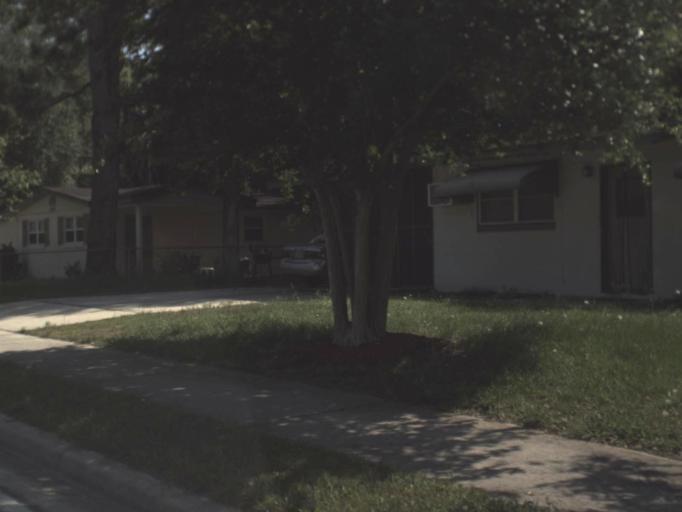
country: US
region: Florida
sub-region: Clay County
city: Bellair-Meadowbrook Terrace
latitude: 30.2756
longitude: -81.7554
